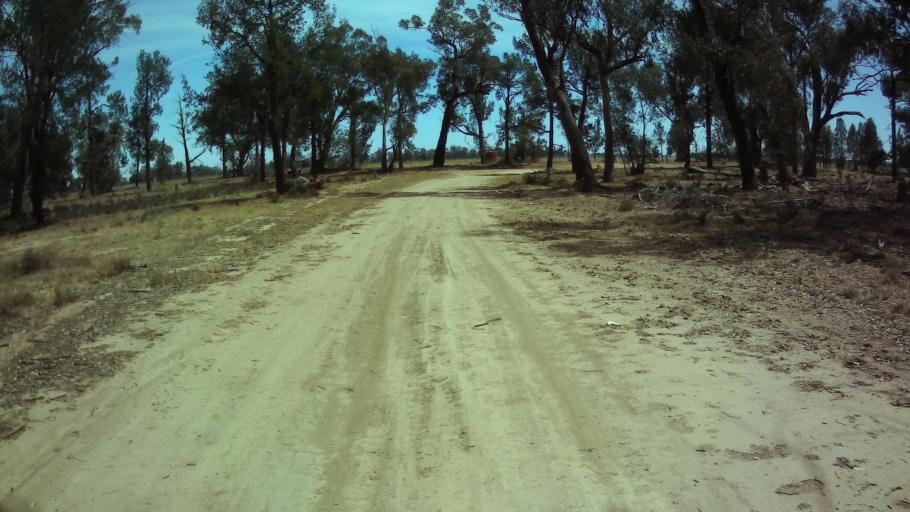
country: AU
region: New South Wales
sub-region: Weddin
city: Grenfell
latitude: -34.0325
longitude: 147.9331
